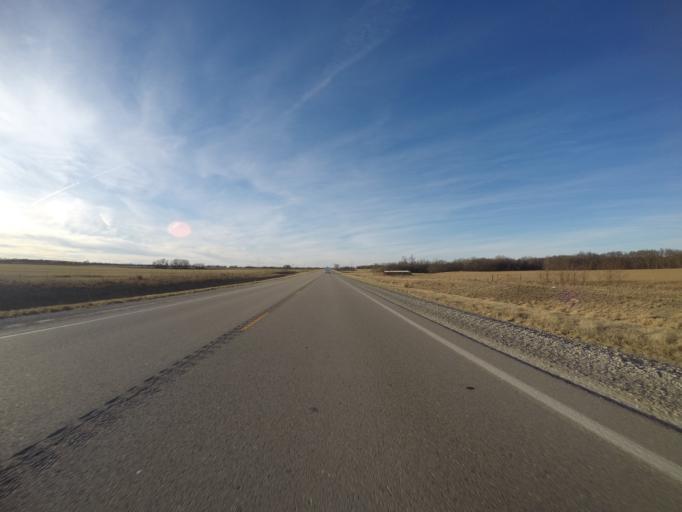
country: US
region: Kansas
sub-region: Marion County
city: Marion
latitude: 38.2494
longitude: -96.9463
